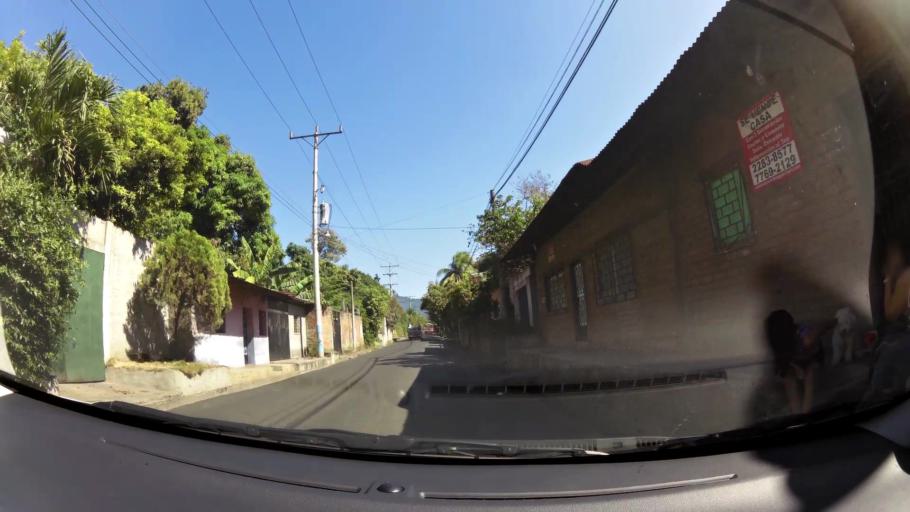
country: SV
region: La Libertad
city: Santa Tecla
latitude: 13.7329
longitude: -89.3763
